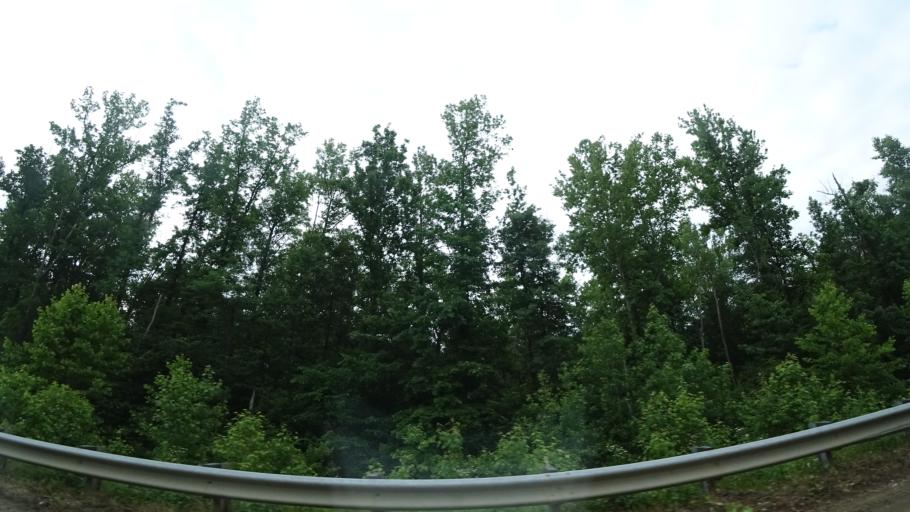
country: US
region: Virginia
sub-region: Spotsylvania County
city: Spotsylvania Courthouse
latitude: 38.1794
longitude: -77.6237
